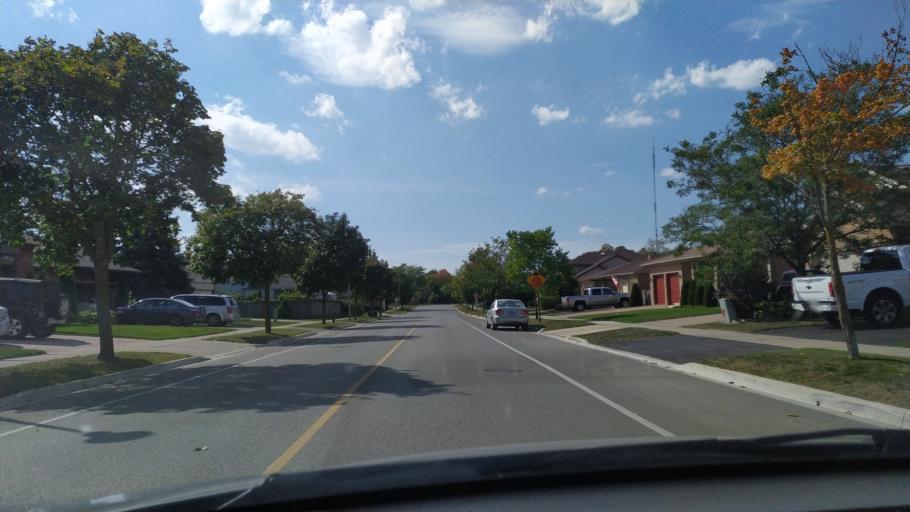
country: CA
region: Ontario
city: London
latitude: 42.9471
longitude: -81.2492
